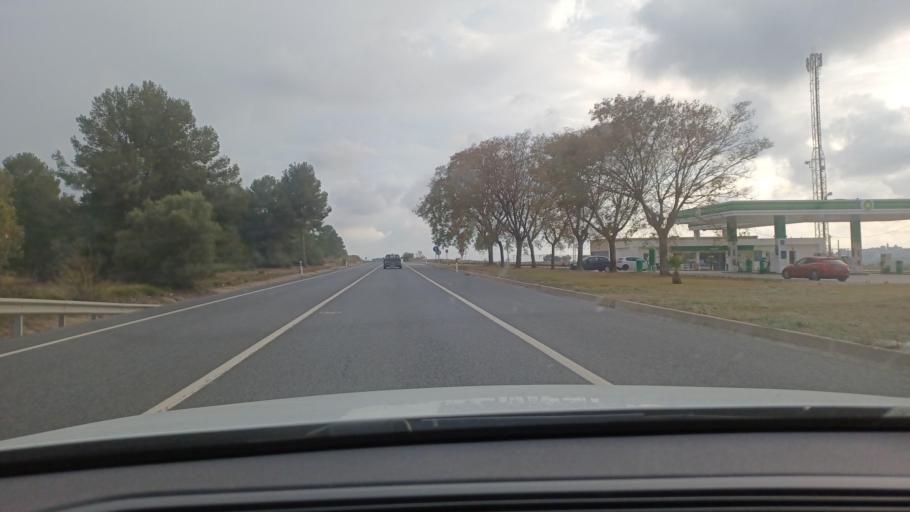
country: ES
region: Catalonia
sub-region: Provincia de Tarragona
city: la Pobla de Mafumet
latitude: 41.1744
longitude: 1.2400
